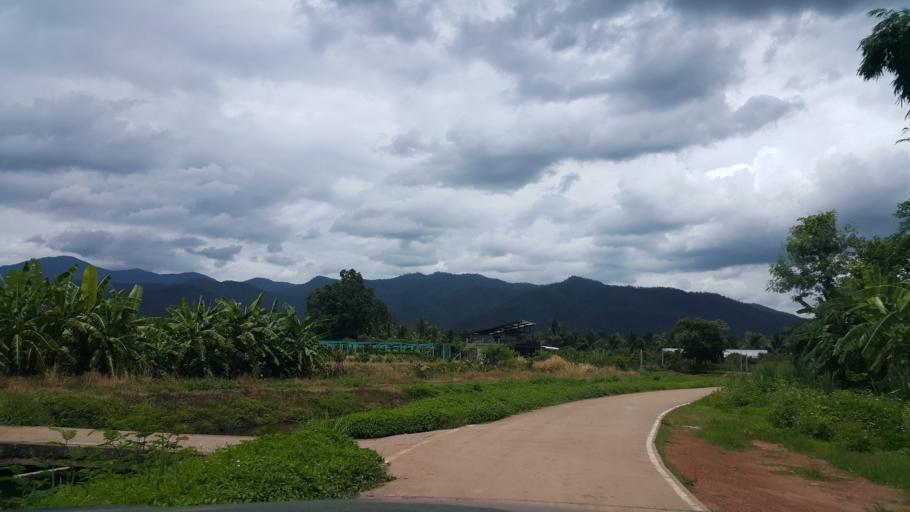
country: TH
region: Chiang Mai
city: Mae Taeng
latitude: 19.2015
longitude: 99.0019
